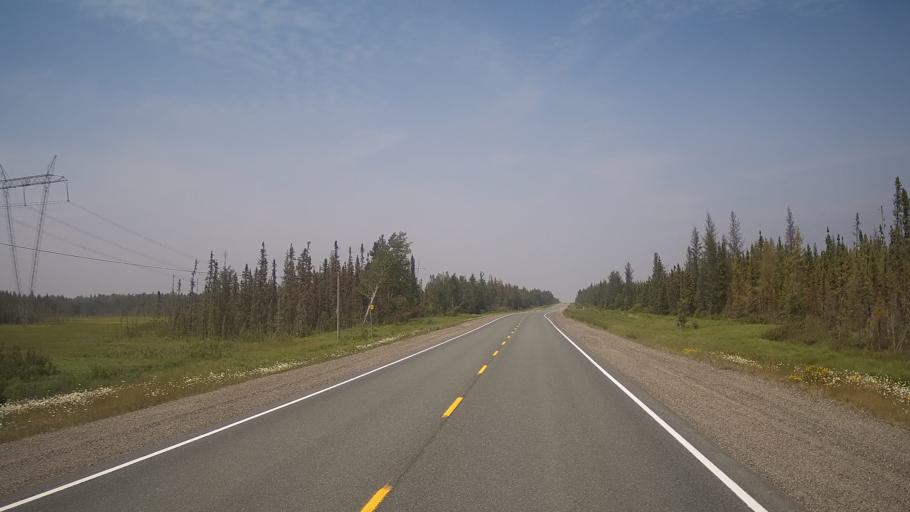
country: CA
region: Ontario
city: Timmins
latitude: 48.7648
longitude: -81.3617
